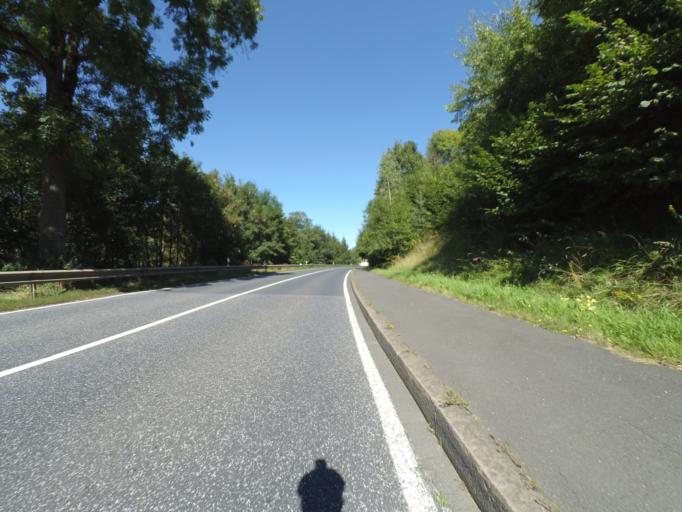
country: DE
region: Rheinland-Pfalz
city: Pelm
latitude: 50.2277
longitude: 6.6805
